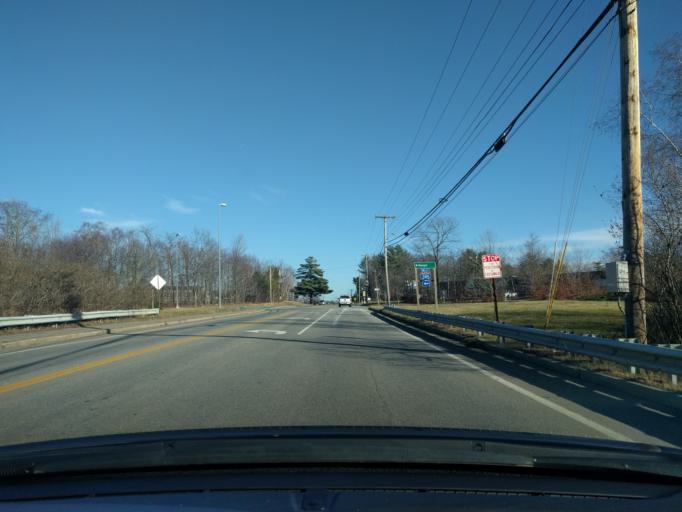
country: US
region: Maine
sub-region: Penobscot County
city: Brewer
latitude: 44.7805
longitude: -68.7582
